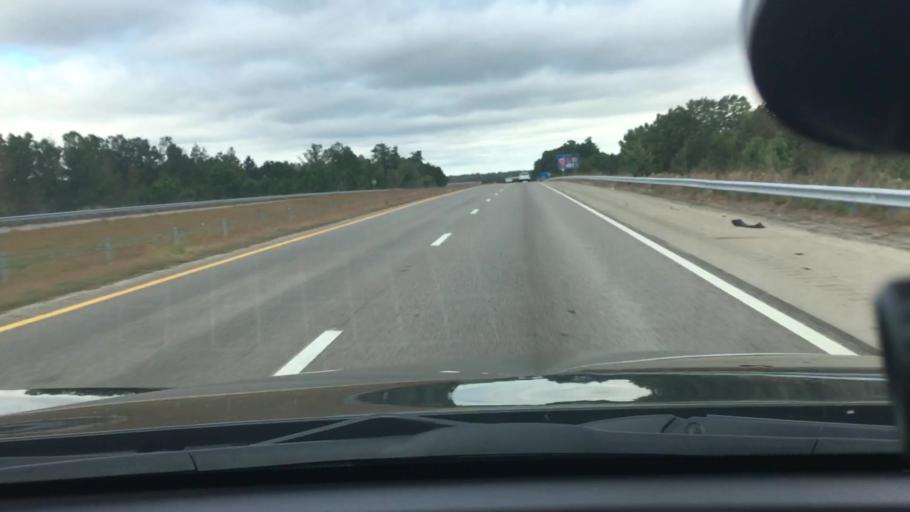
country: US
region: North Carolina
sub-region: Wilson County
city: Lucama
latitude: 35.7525
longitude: -78.0237
